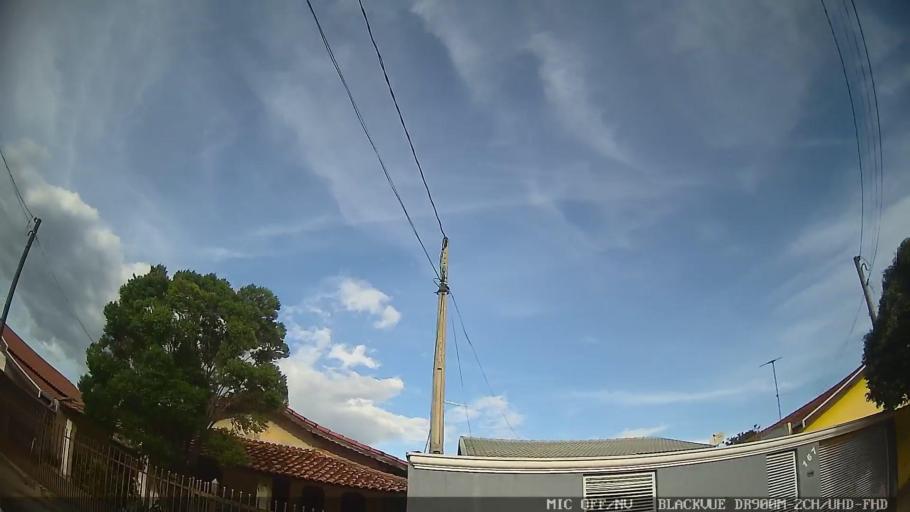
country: BR
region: Sao Paulo
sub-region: Jaguariuna
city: Jaguariuna
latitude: -22.6437
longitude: -47.0530
